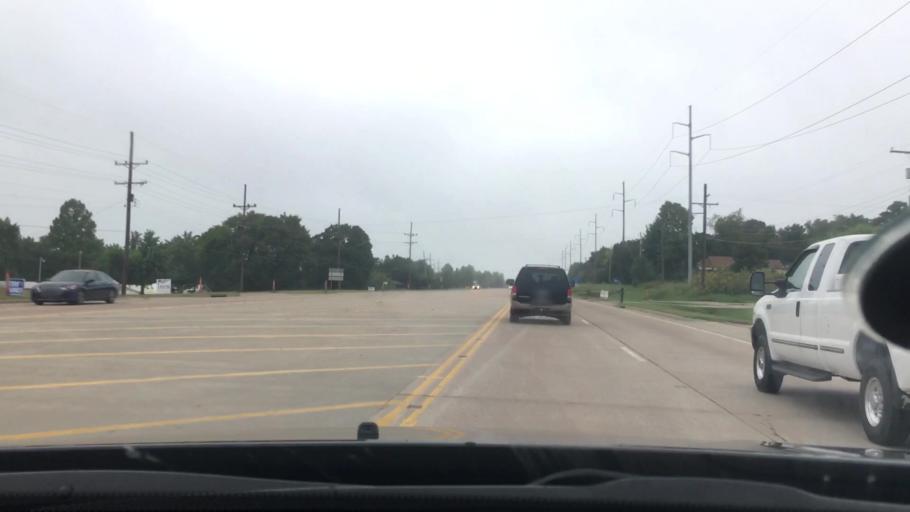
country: US
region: Oklahoma
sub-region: Seminole County
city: Seminole
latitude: 35.2478
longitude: -96.6710
